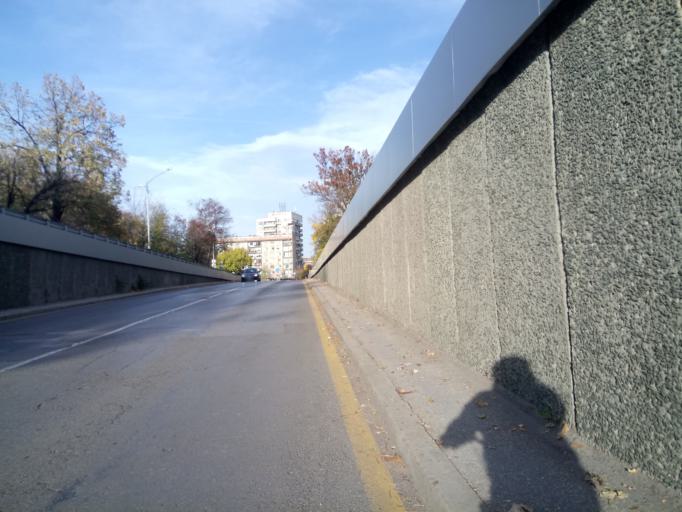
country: BG
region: Sofia-Capital
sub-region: Stolichna Obshtina
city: Sofia
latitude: 42.6790
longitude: 23.3551
